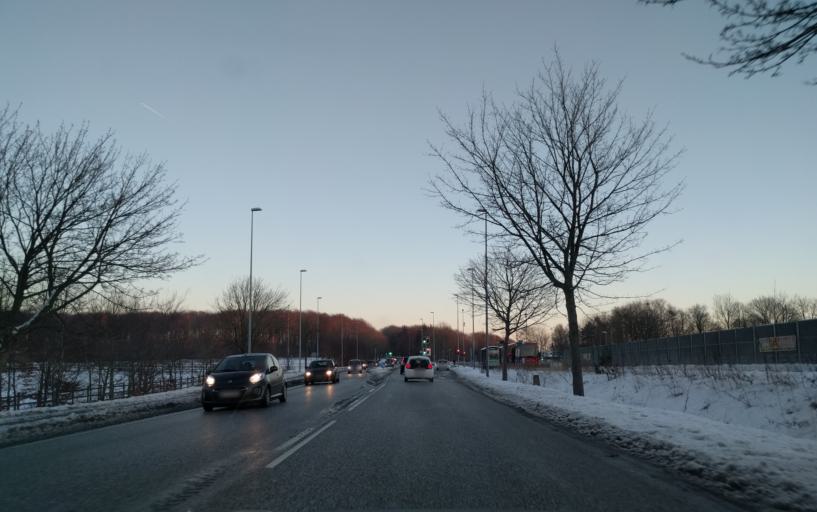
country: DK
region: North Denmark
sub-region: Alborg Kommune
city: Aalborg
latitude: 57.0218
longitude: 9.9505
